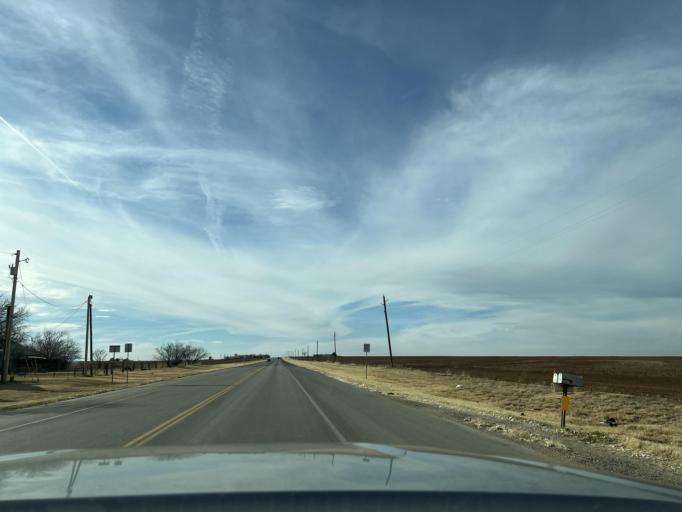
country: US
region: Texas
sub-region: Jones County
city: Anson
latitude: 32.7517
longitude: -99.9071
